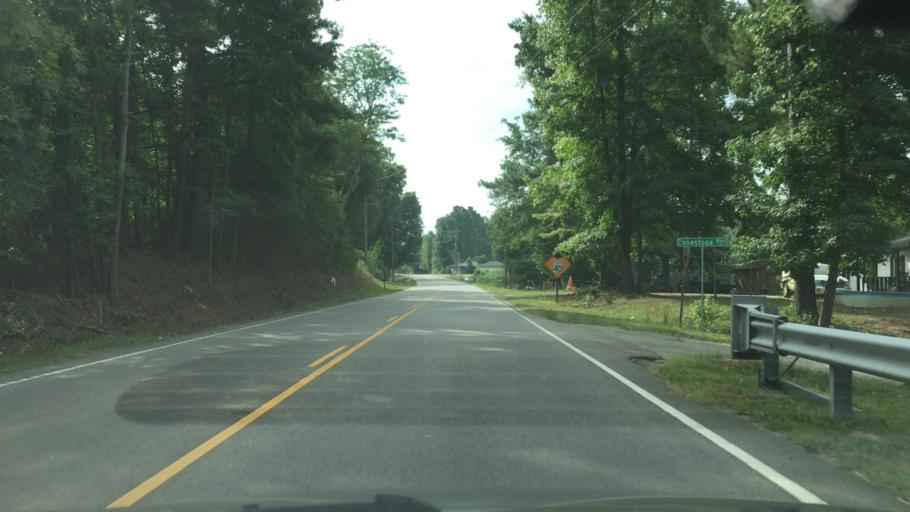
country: US
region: South Carolina
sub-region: Barnwell County
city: Williston
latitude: 33.6553
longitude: -81.3739
